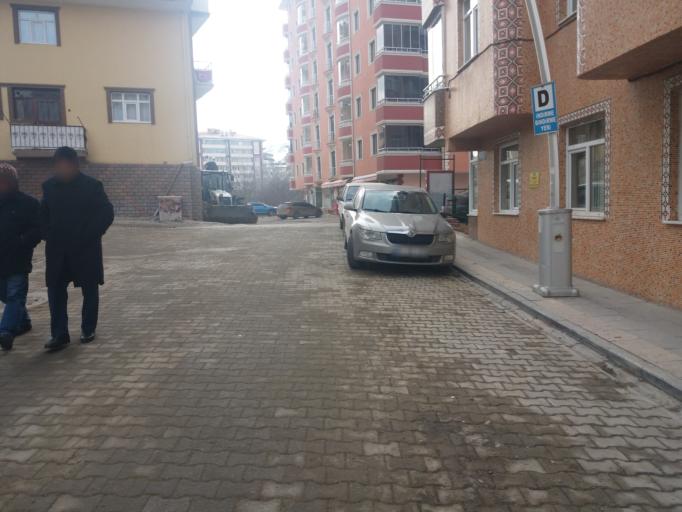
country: TR
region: Gumushane
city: Gumushkhane
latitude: 40.4556
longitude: 39.4892
